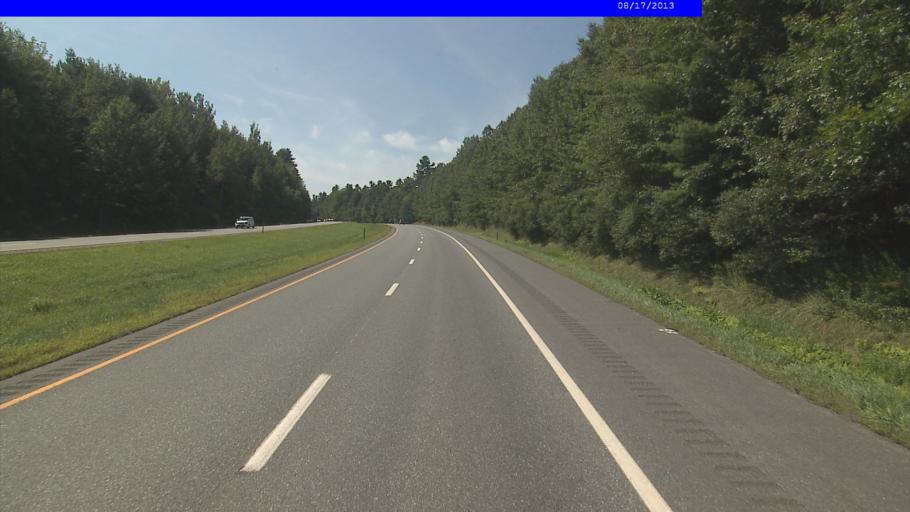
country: US
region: Vermont
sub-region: Windham County
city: Brattleboro
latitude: 42.8685
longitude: -72.5786
